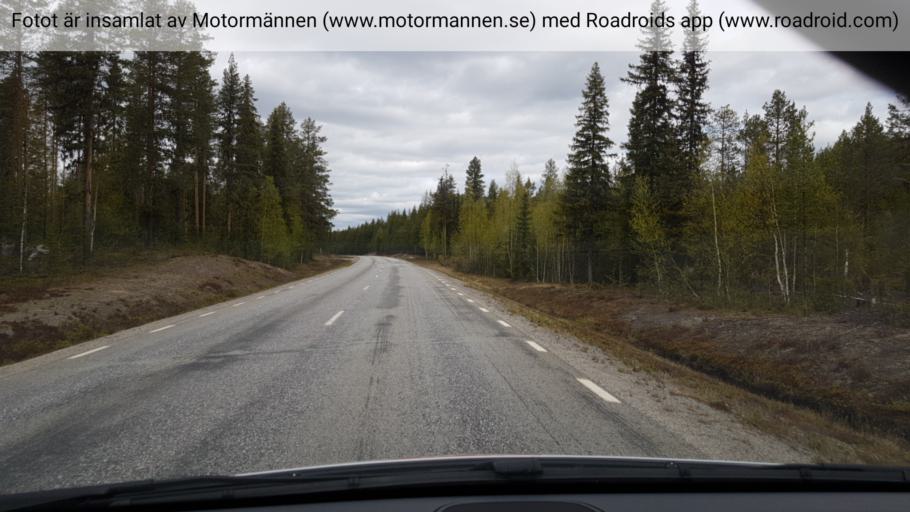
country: SE
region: Vaesterbotten
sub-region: Mala Kommun
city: Mala
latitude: 64.9455
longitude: 18.6191
